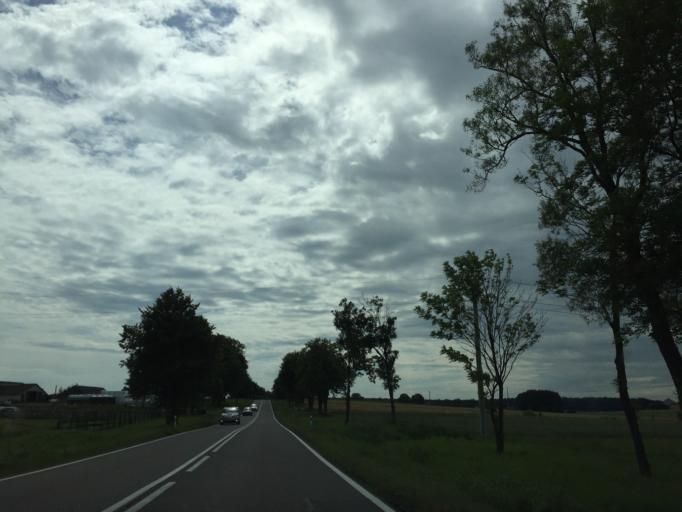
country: PL
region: Podlasie
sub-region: Powiat siemiatycki
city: Dziadkowice
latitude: 52.6024
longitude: 22.9735
